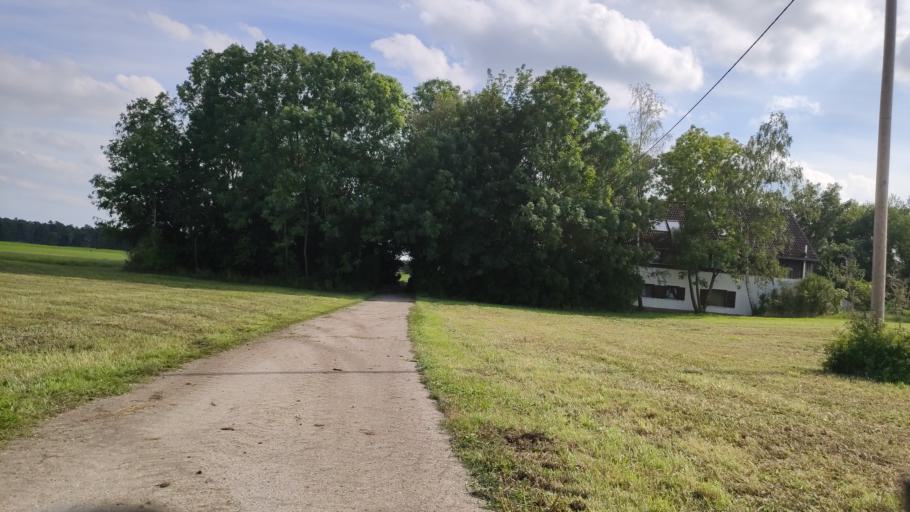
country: DE
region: Bavaria
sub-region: Upper Bavaria
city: Hurlach
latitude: 48.1326
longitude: 10.8370
